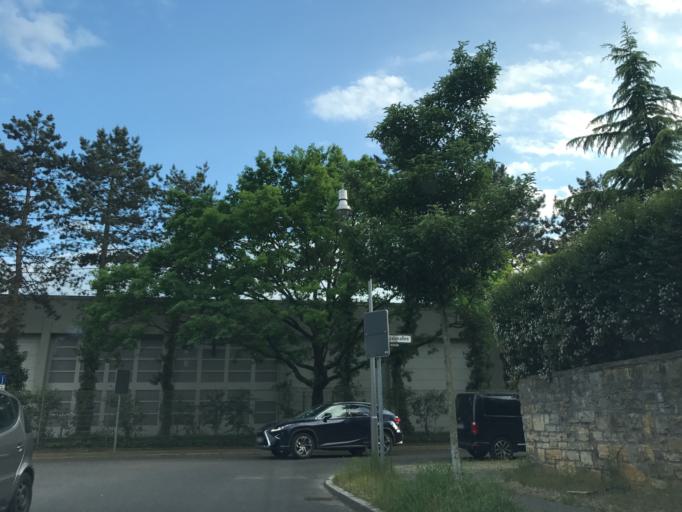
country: DE
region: Berlin
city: Westend
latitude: 52.5061
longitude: 13.2690
